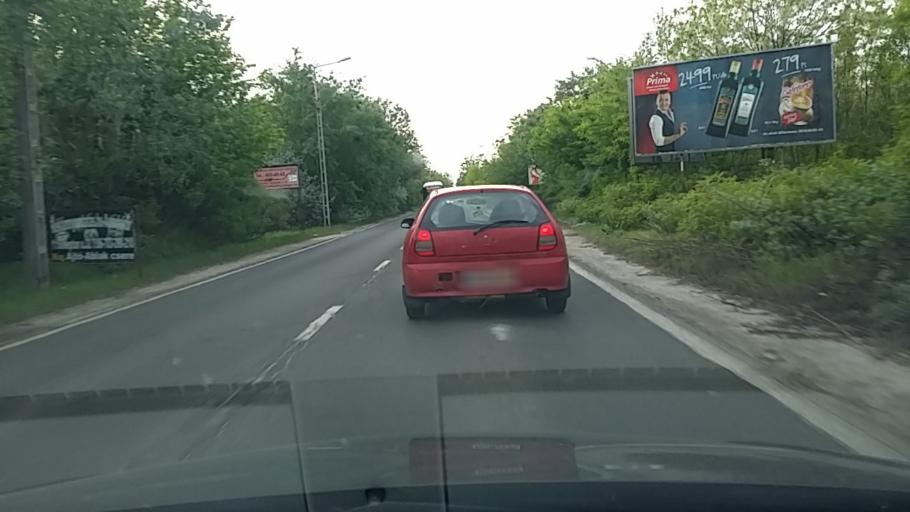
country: HU
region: Budapest
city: Budapest XVI. keruelet
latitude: 47.5380
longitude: 19.1585
